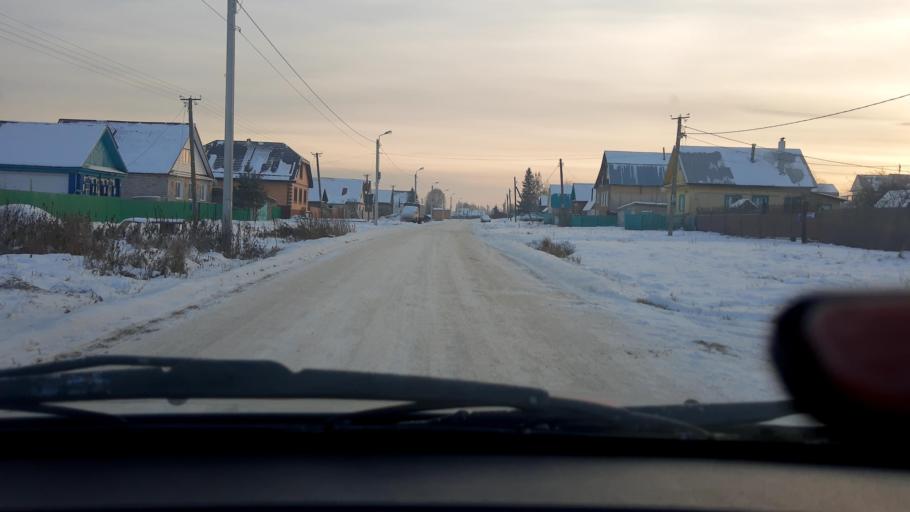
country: RU
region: Bashkortostan
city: Mikhaylovka
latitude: 54.7508
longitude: 55.7992
